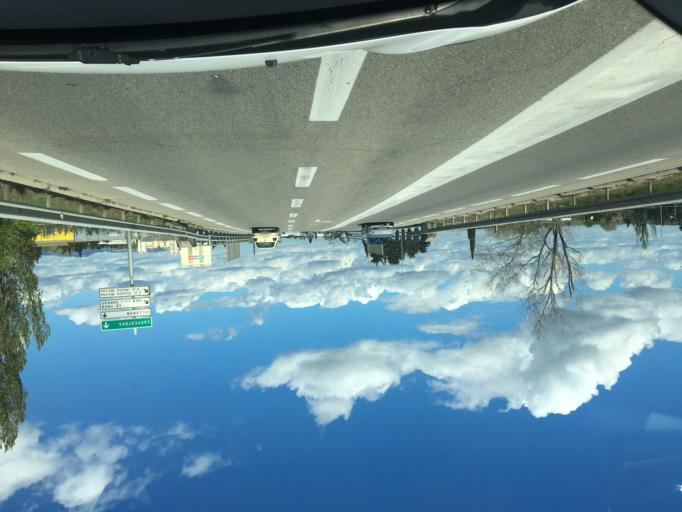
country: FR
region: Provence-Alpes-Cote d'Azur
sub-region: Departement du Vaucluse
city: L'Isle-sur-la-Sorgue
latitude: 43.9182
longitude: 5.0296
